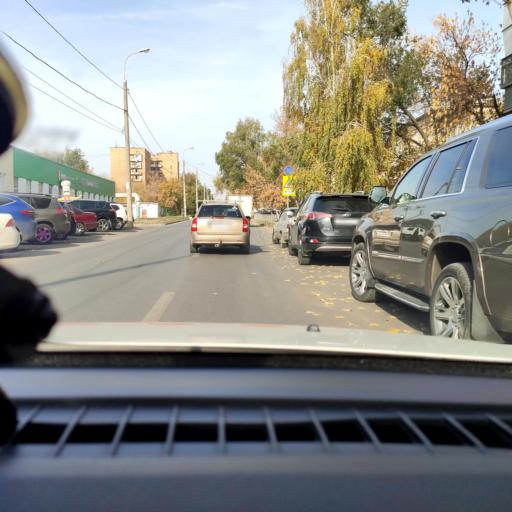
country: RU
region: Samara
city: Samara
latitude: 53.1883
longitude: 50.1743
